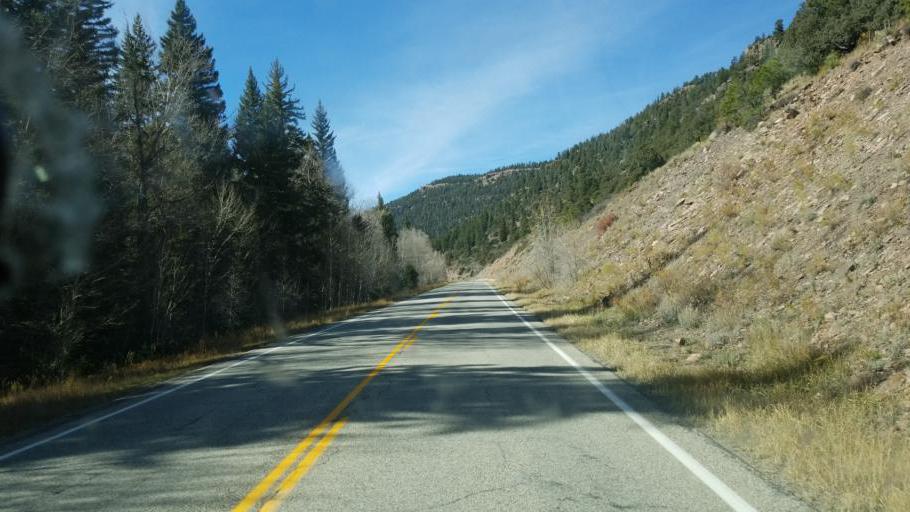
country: US
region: Colorado
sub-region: Conejos County
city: Conejos
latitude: 37.0694
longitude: -106.2523
